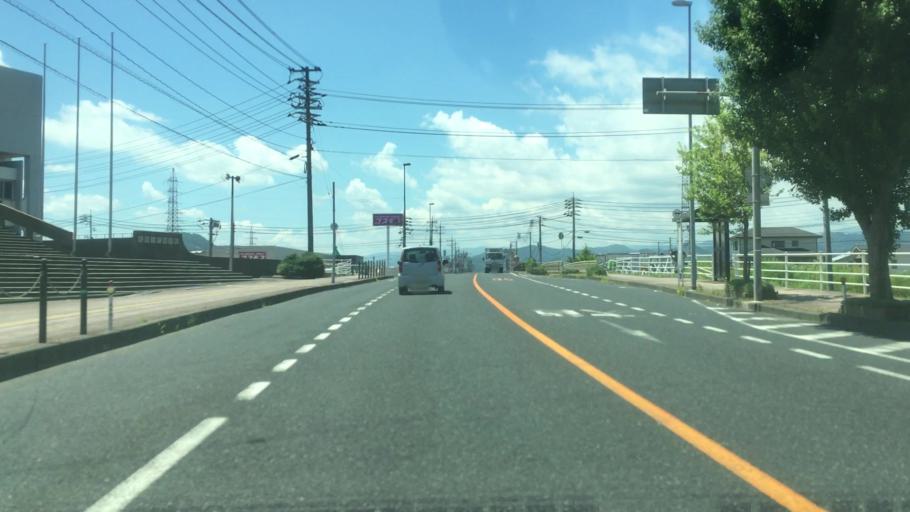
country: JP
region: Tottori
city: Tottori
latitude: 35.4846
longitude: 134.2206
